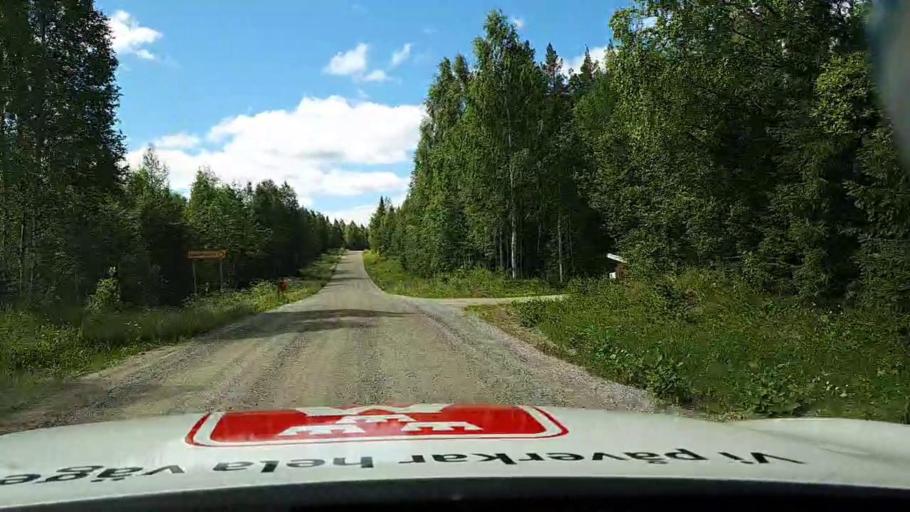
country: SE
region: Jaemtland
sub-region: Braecke Kommun
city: Braecke
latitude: 62.7443
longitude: 15.5014
